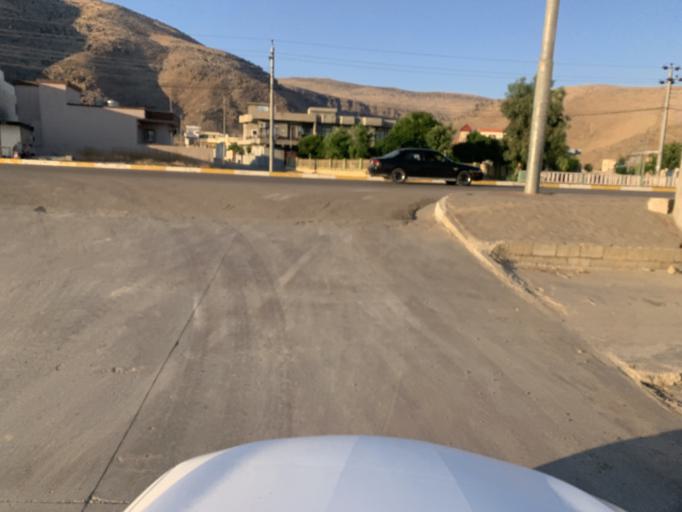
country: IQ
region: As Sulaymaniyah
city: Raniye
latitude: 36.2713
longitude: 44.7604
